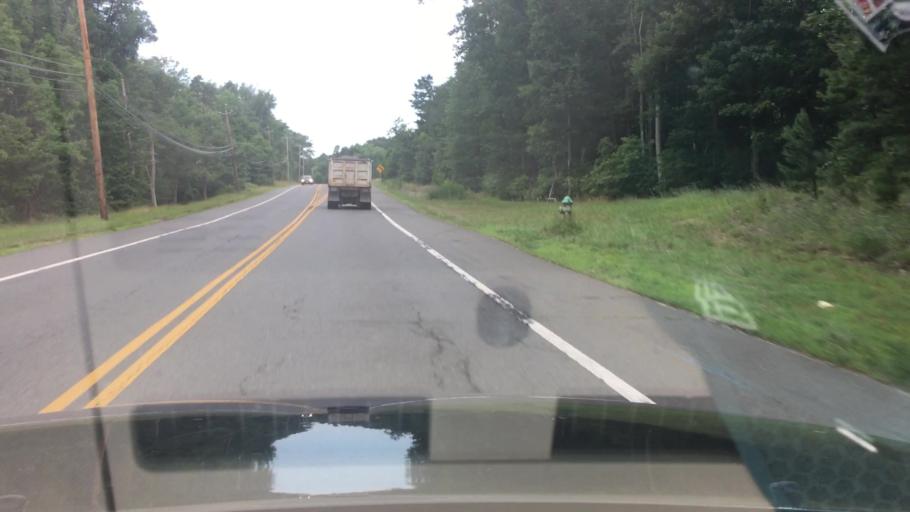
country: US
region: New Jersey
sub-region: Ocean County
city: Lakehurst
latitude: 40.0653
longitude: -74.3617
